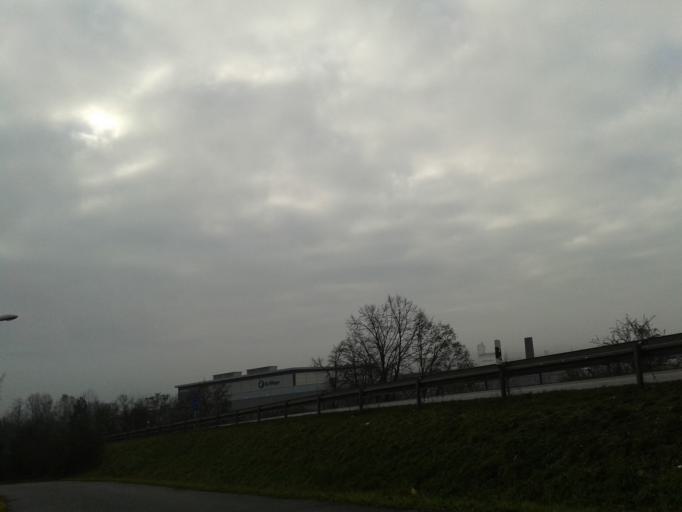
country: DE
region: Bavaria
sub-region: Upper Franconia
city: Hallstadt
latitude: 49.9161
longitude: 10.8766
